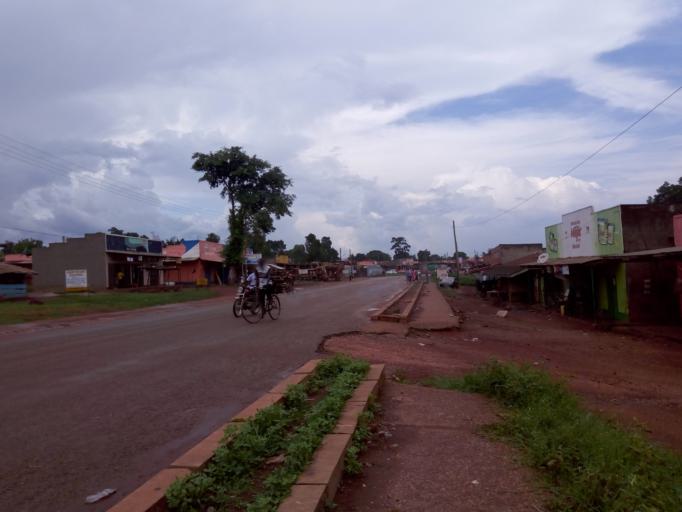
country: UG
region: Western Region
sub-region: Masindi District
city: Masindi
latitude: 1.6918
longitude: 31.7084
